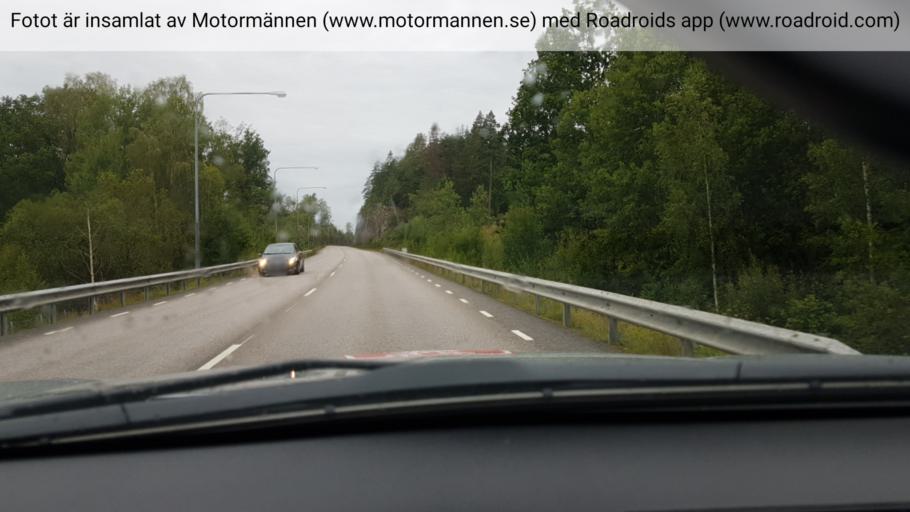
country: SE
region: Vaestra Goetaland
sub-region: Trollhattan
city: Trollhattan
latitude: 58.3128
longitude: 12.2835
